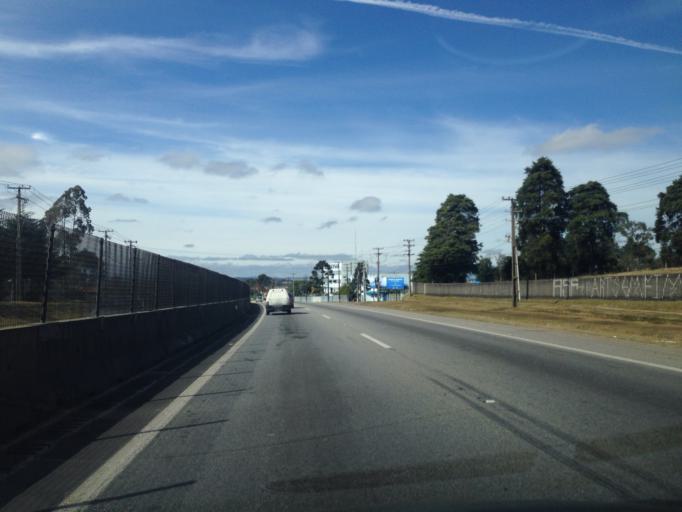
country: BR
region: Parana
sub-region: Pinhais
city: Pinhais
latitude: -25.4761
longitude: -49.2070
